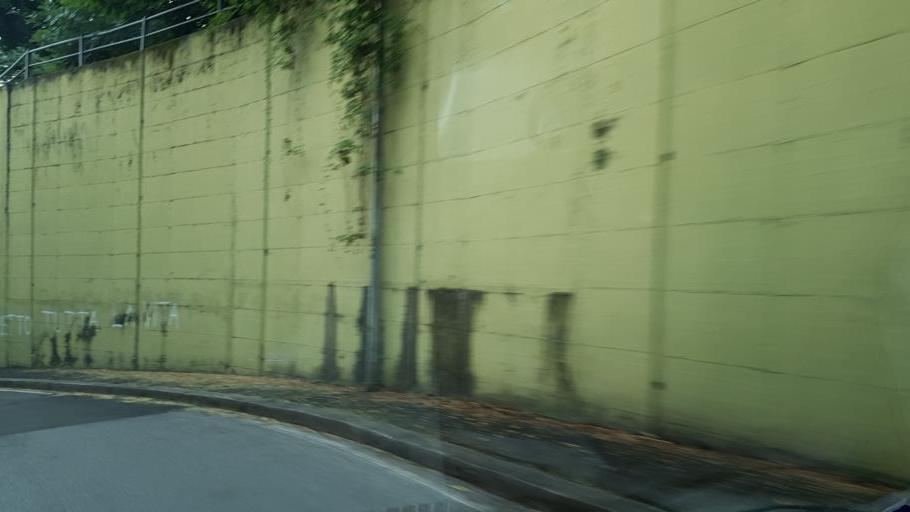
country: IT
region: Liguria
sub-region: Provincia di Genova
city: San Teodoro
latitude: 44.4293
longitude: 8.8322
